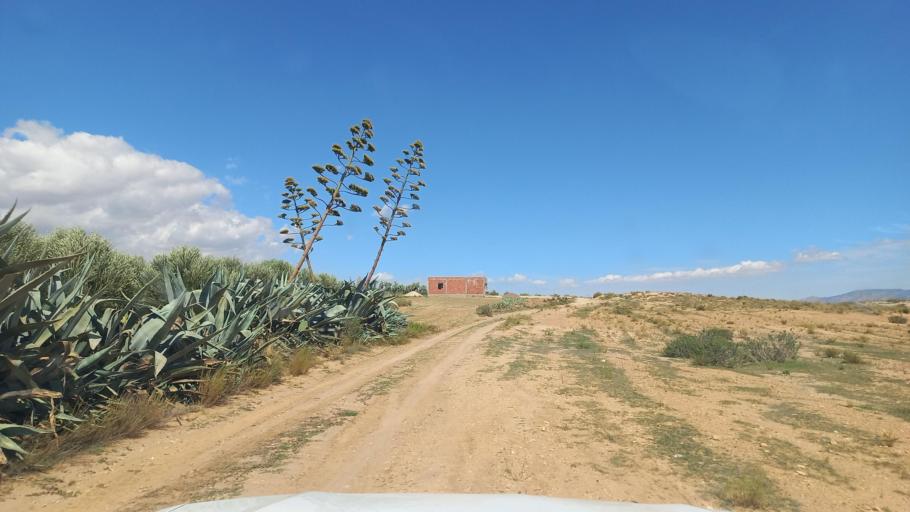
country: TN
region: Al Qasrayn
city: Sbiba
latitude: 35.3494
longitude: 9.0164
